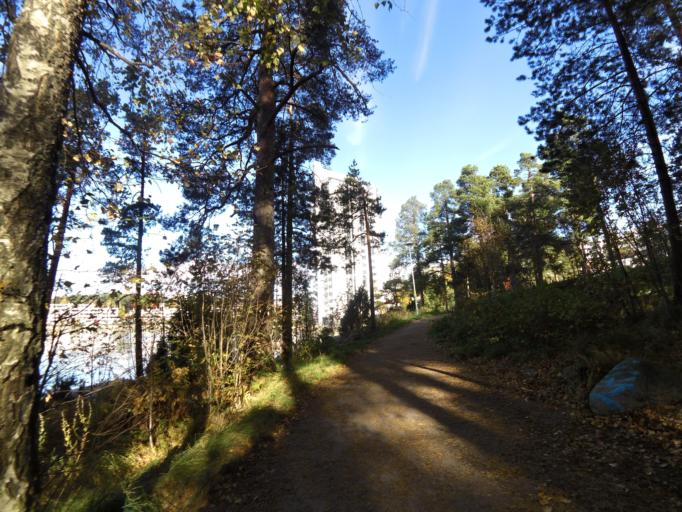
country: FI
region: Uusimaa
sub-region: Helsinki
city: Espoo
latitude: 60.1496
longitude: 24.6340
